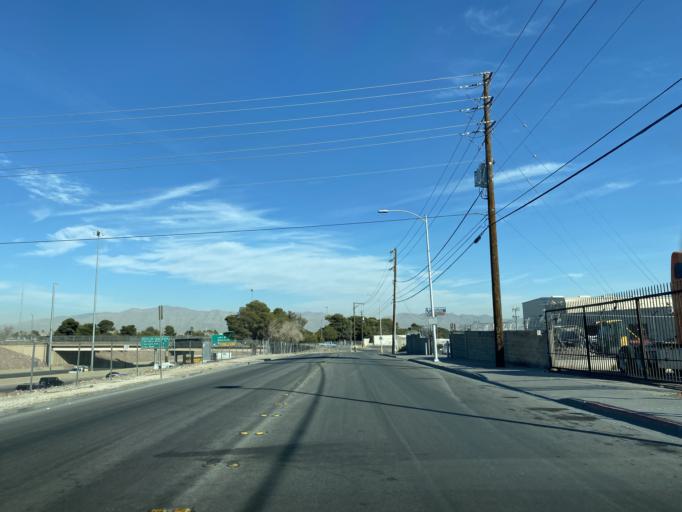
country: US
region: Nevada
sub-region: Clark County
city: Las Vegas
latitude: 36.1868
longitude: -115.1430
